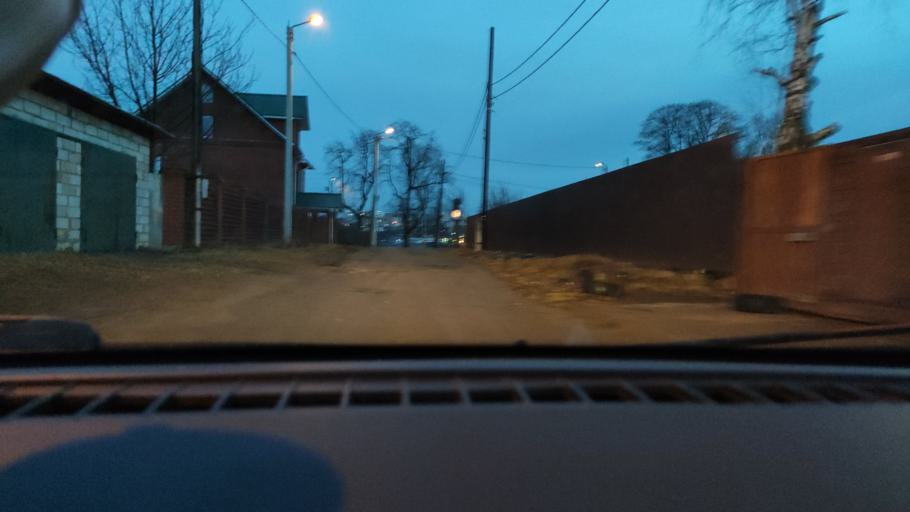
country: RU
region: Perm
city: Perm
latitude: 58.0330
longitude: 56.2494
